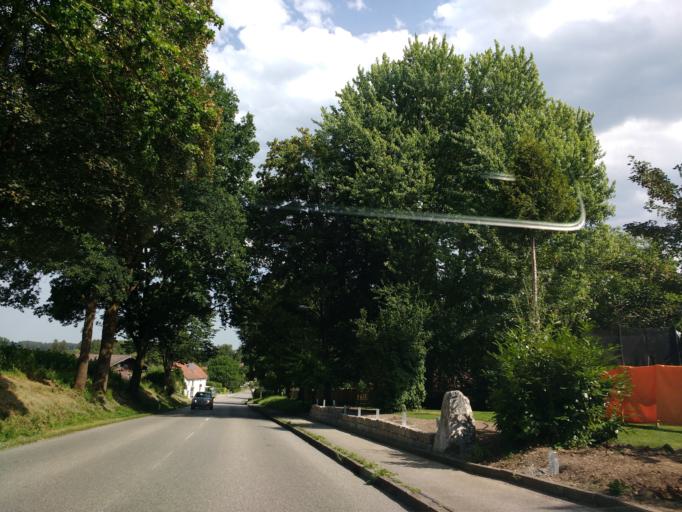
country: DE
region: Bavaria
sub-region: Upper Bavaria
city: Kienberg
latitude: 48.0349
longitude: 12.4637
